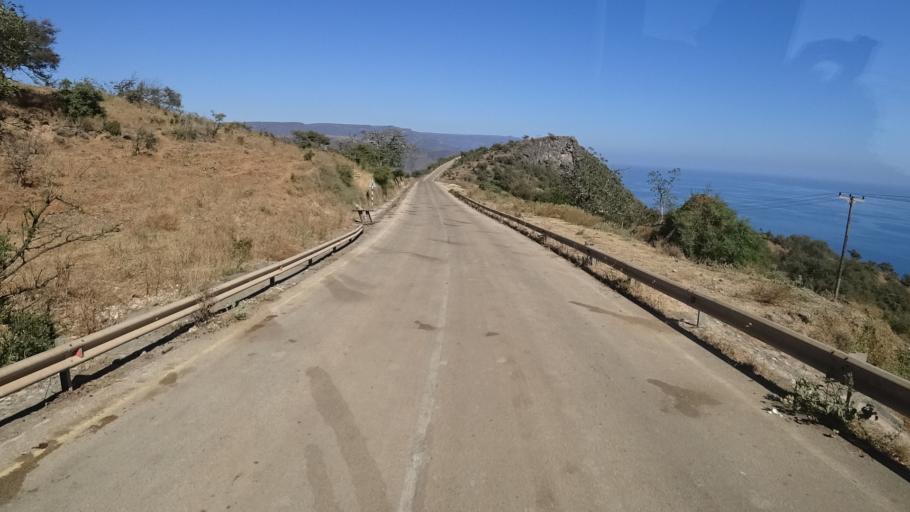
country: YE
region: Al Mahrah
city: Hawf
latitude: 16.7433
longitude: 53.3818
